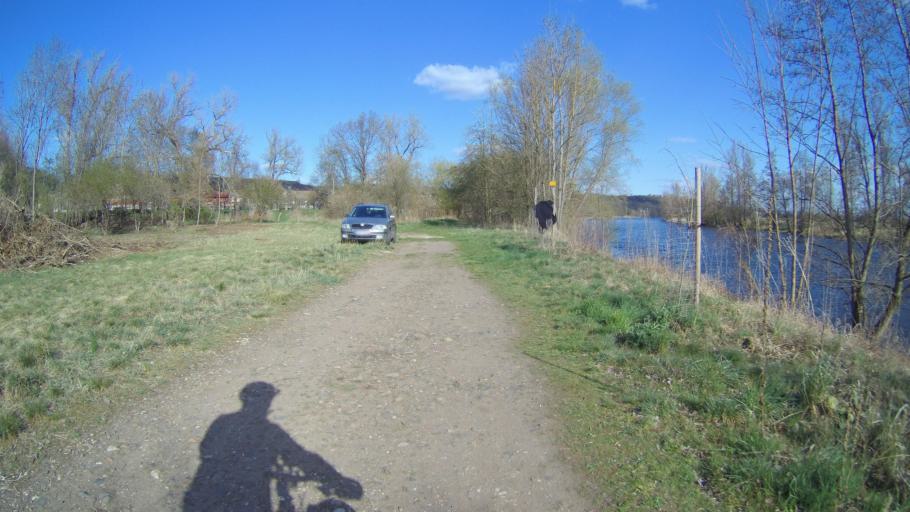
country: CZ
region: Ustecky
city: Zatec
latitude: 50.3553
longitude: 13.4944
